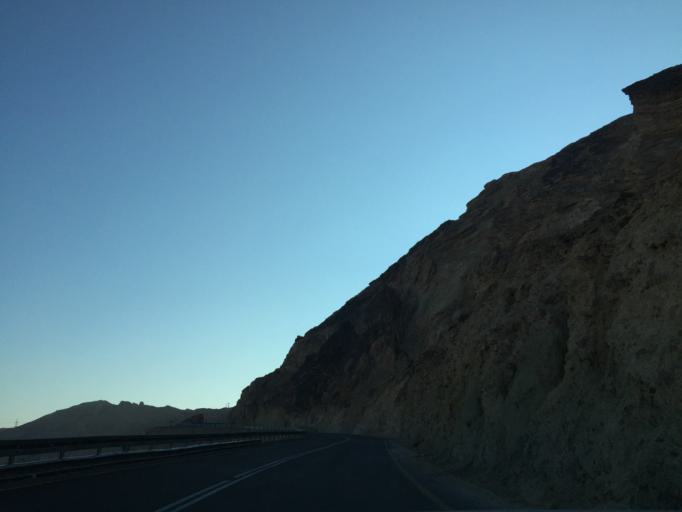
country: IL
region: Southern District
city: Mitzpe Ramon
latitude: 30.3208
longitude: 34.9591
